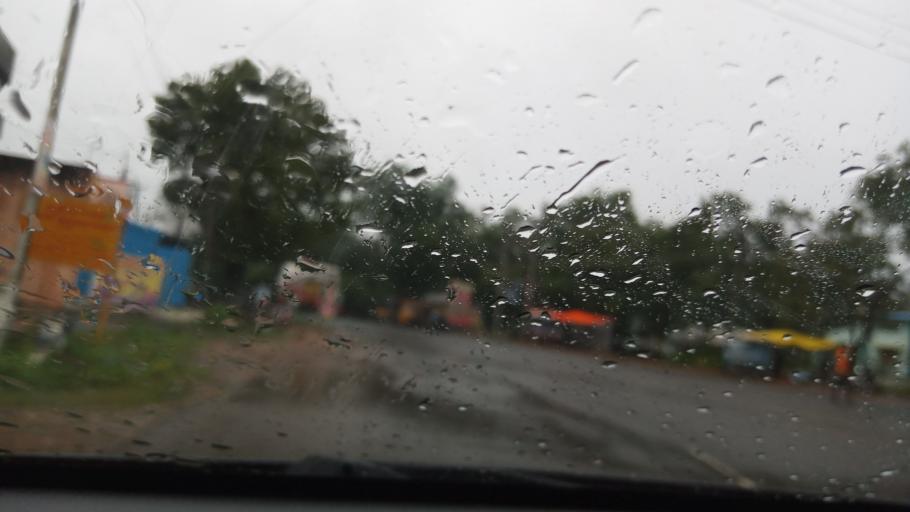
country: IN
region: Tamil Nadu
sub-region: Tiruvannamalai
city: Cheyyar
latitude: 12.6763
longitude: 79.5364
